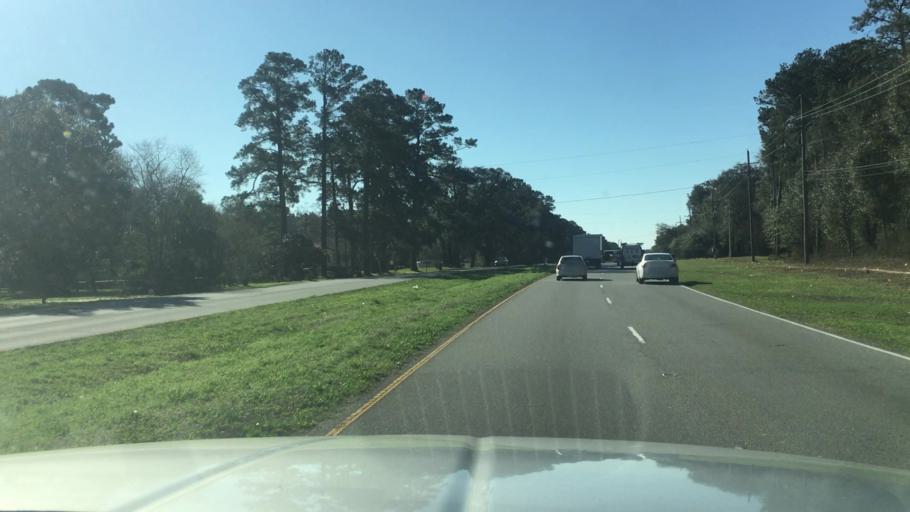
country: US
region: North Carolina
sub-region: New Hanover County
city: Sea Breeze
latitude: 34.0946
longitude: -77.8977
